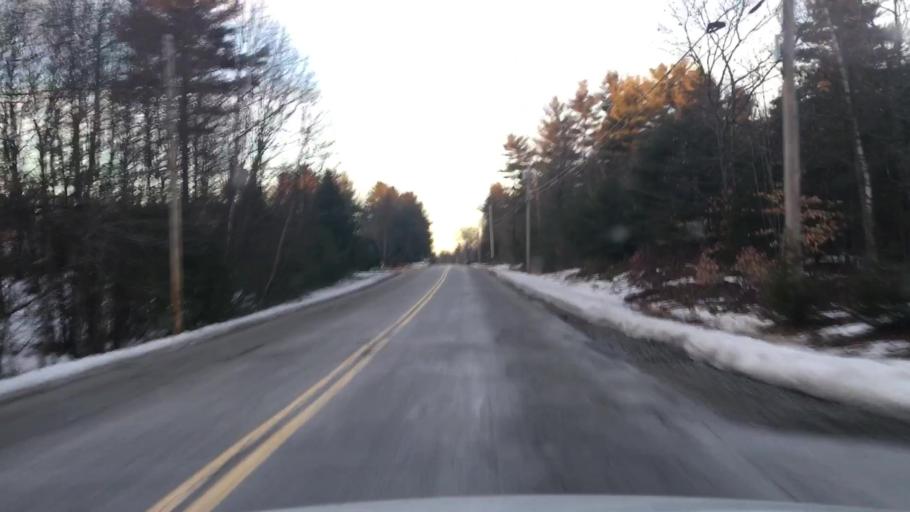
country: US
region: Maine
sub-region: York County
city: Lebanon
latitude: 43.3475
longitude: -70.8660
